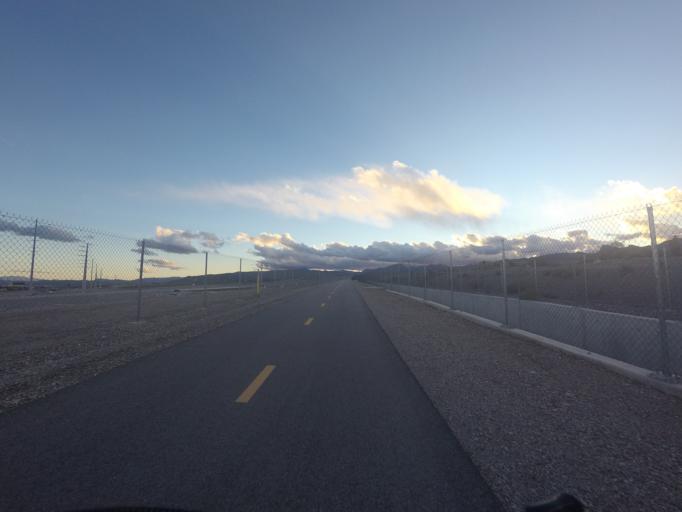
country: US
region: Nevada
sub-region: Clark County
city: Summerlin South
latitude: 36.1940
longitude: -115.3441
